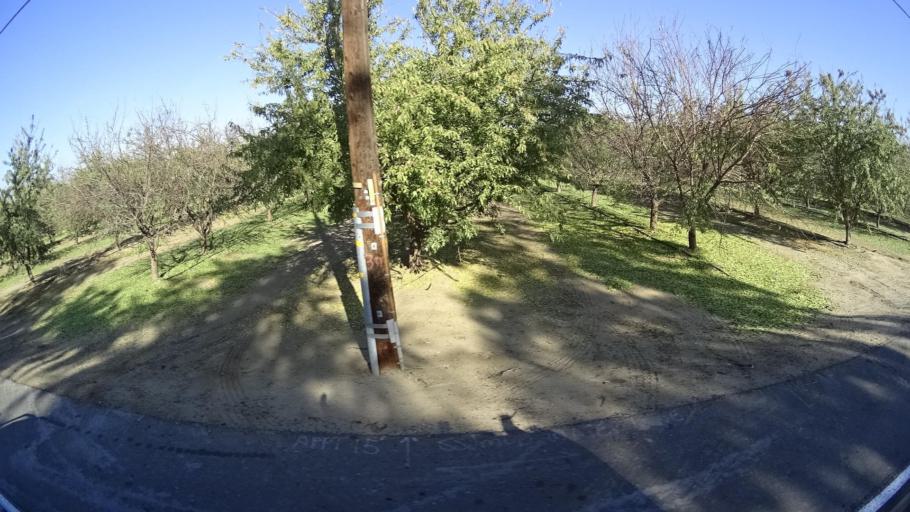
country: US
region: California
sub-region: Kern County
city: Delano
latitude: 35.7178
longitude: -119.3126
